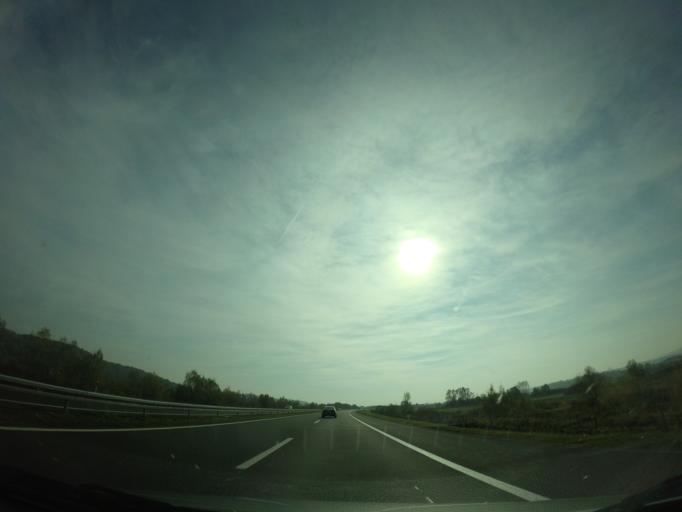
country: HR
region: Varazdinska
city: Remetinec
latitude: 46.0118
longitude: 16.2945
